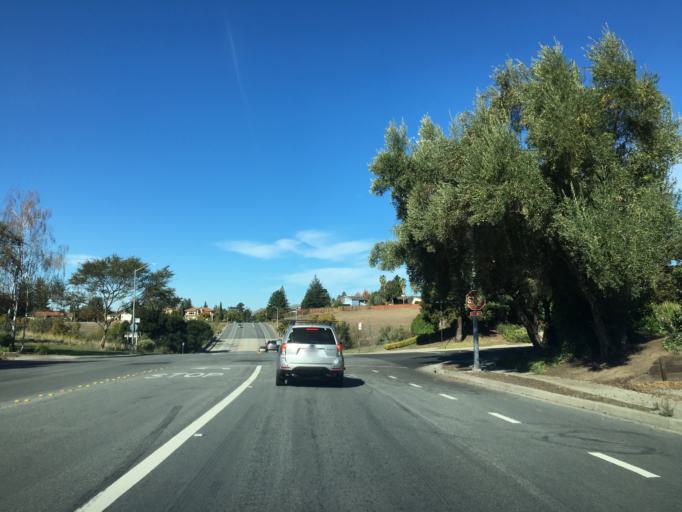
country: US
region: California
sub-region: Alameda County
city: Fremont
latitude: 37.5259
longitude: -121.9292
